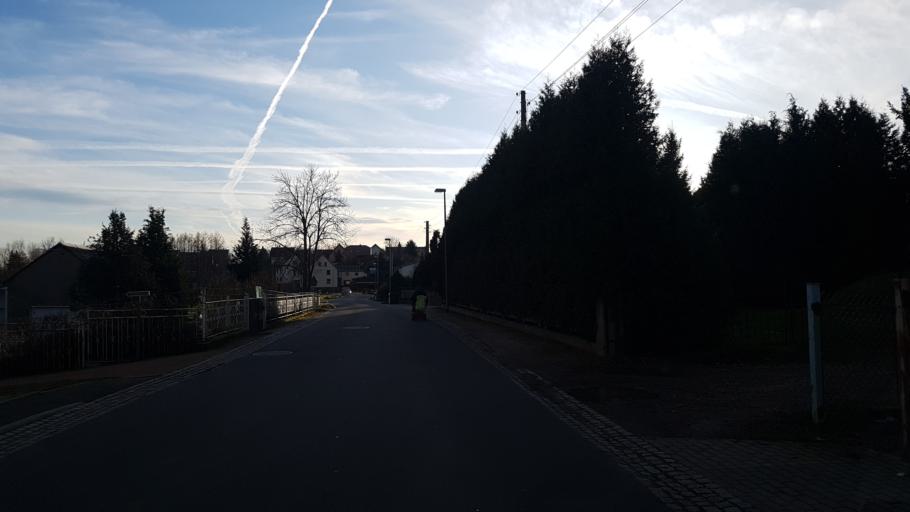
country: DE
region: Saxony
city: Ostrau
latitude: 51.1727
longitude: 13.1628
